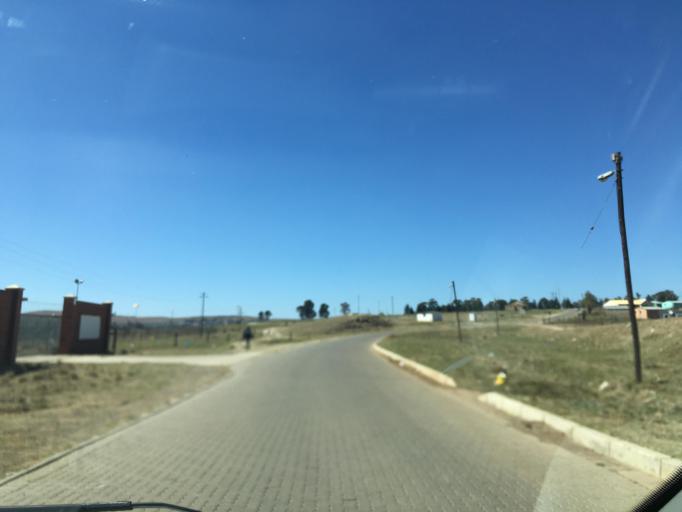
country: ZA
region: Eastern Cape
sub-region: Chris Hani District Municipality
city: Elliot
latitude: -31.3314
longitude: 27.8318
